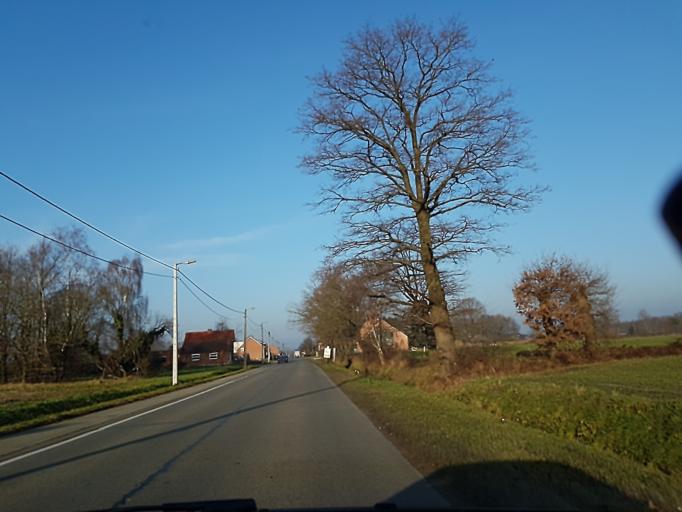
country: BE
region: Flanders
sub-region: Provincie Vlaams-Brabant
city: Tremelo
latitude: 51.0265
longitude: 4.7109
